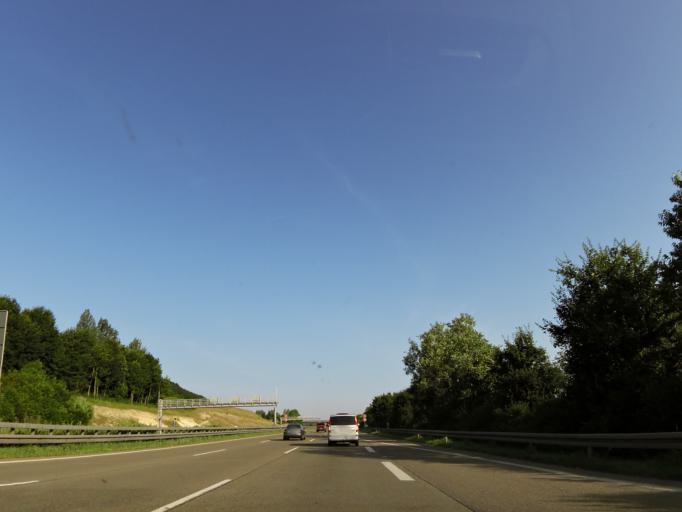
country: DE
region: Baden-Wuerttemberg
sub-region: Regierungsbezirk Stuttgart
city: Gruibingen
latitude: 48.6095
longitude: 9.6278
